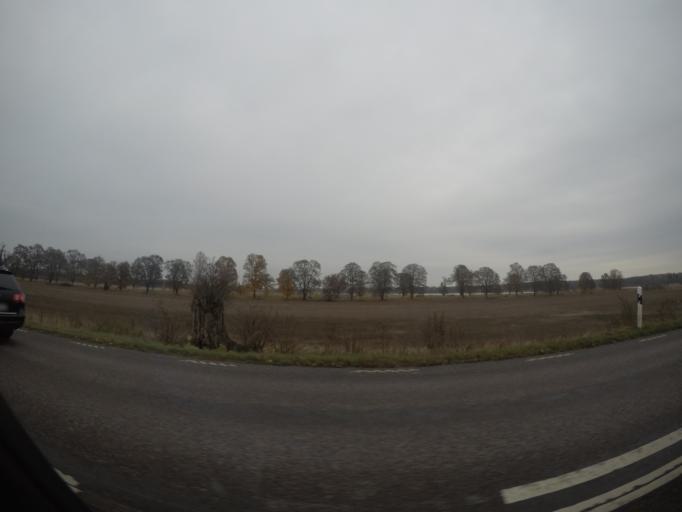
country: SE
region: Vaestmanland
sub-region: Hallstahammars Kommun
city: Kolback
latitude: 59.5152
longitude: 16.2596
